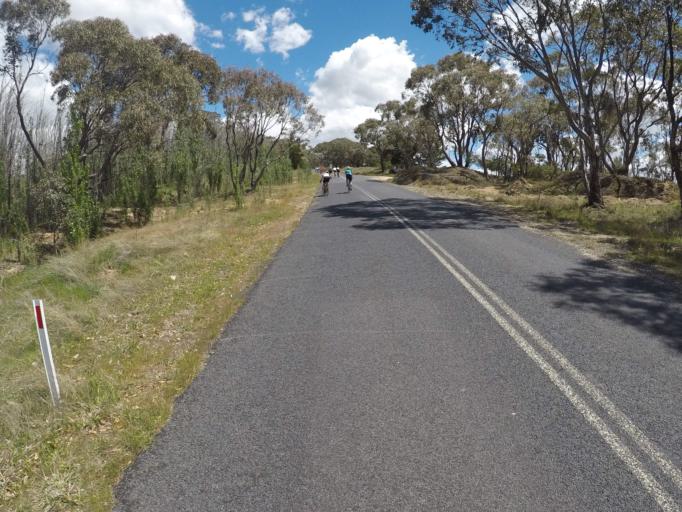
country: AU
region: New South Wales
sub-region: Blayney
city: Blayney
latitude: -33.5795
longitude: 149.3992
